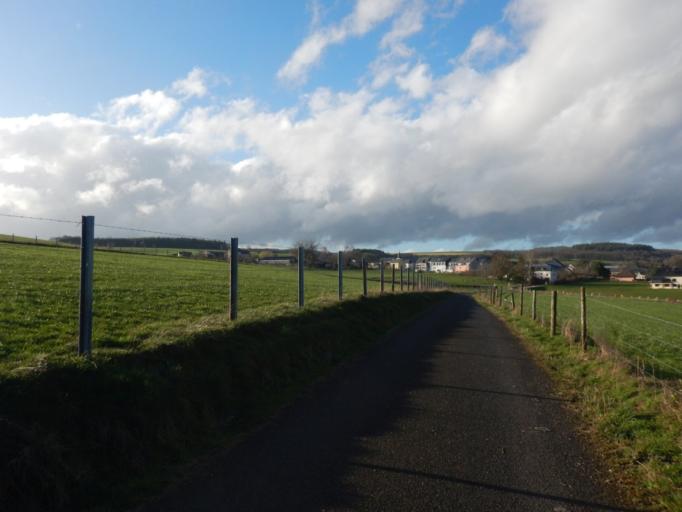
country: BE
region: Wallonia
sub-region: Province du Luxembourg
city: Attert
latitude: 49.7755
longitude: 5.8125
